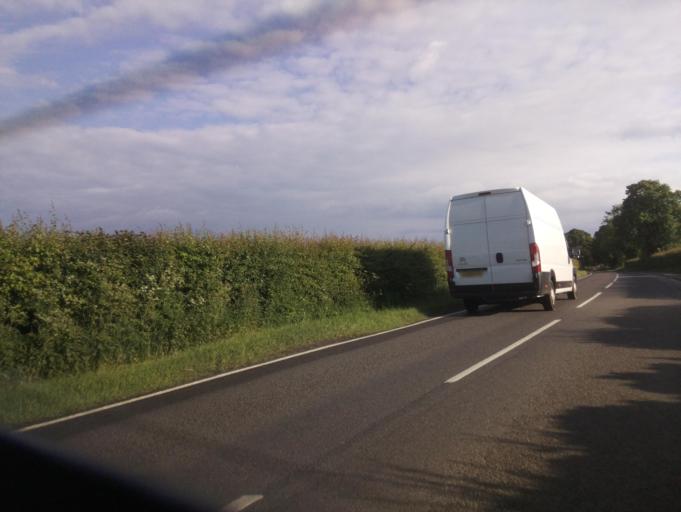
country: GB
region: England
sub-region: Lincolnshire
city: Navenby
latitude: 53.0636
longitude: -0.6369
